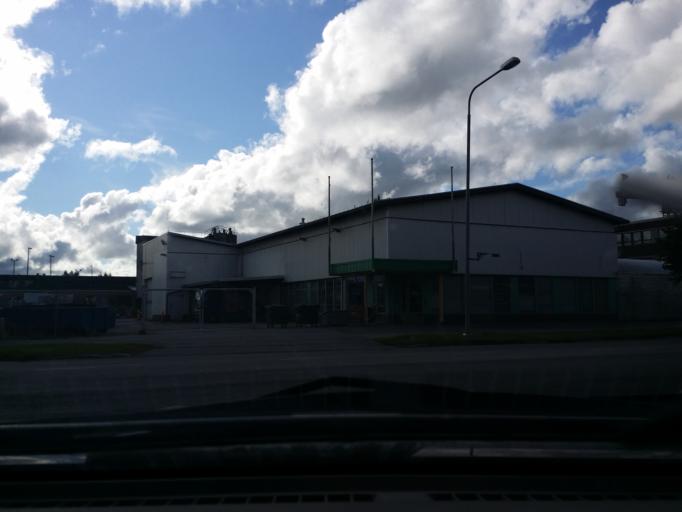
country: FI
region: Satakunta
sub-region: Pori
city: Pori
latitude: 61.4717
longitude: 21.8019
